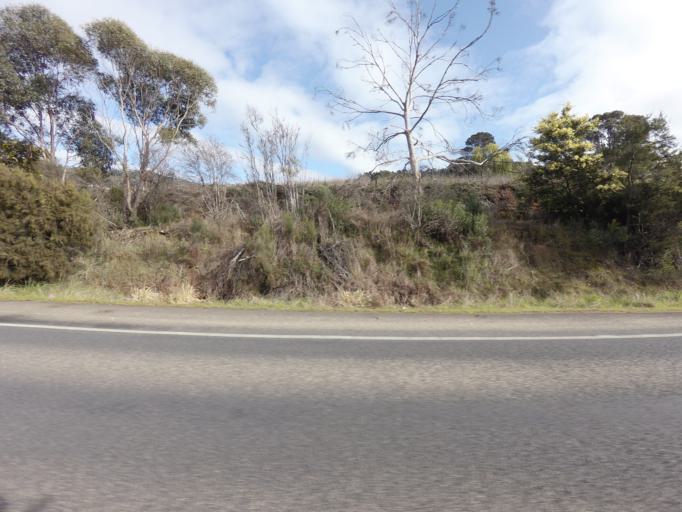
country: AU
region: Tasmania
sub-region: Huon Valley
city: Huonville
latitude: -43.0560
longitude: 147.0324
